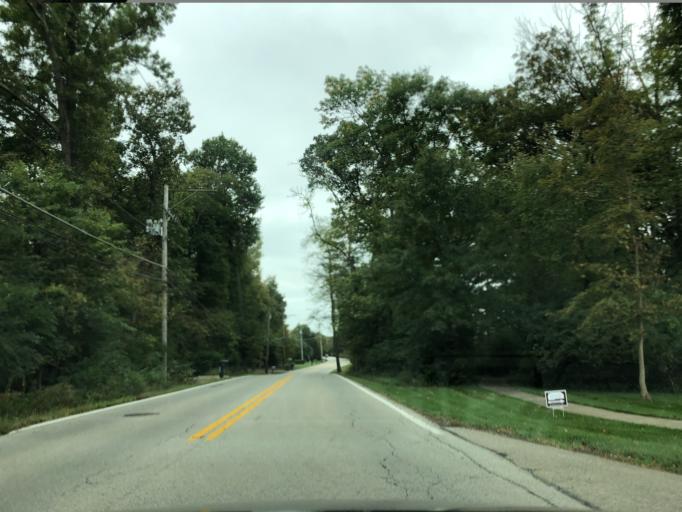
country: US
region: Ohio
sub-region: Hamilton County
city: Sixteen Mile Stand
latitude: 39.2661
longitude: -84.3087
